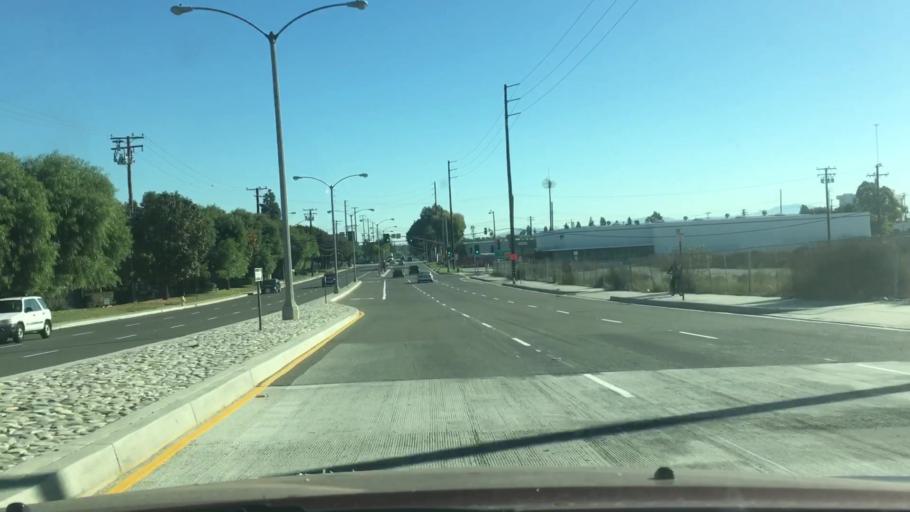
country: US
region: California
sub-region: Los Angeles County
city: La Mirada
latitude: 33.8879
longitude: -118.0329
